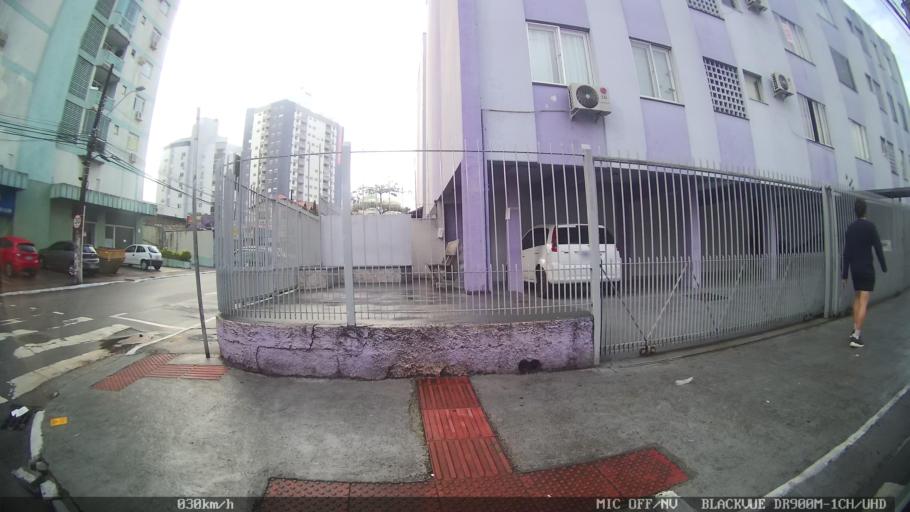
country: BR
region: Santa Catarina
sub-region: Sao Jose
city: Campinas
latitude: -27.5937
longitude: -48.6131
